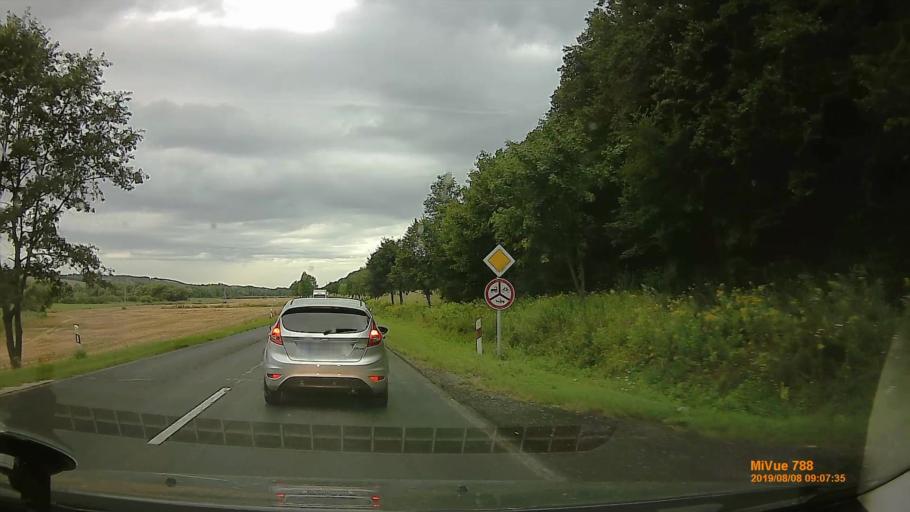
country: HU
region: Zala
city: Zalaegerszeg
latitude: 46.7354
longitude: 16.8560
